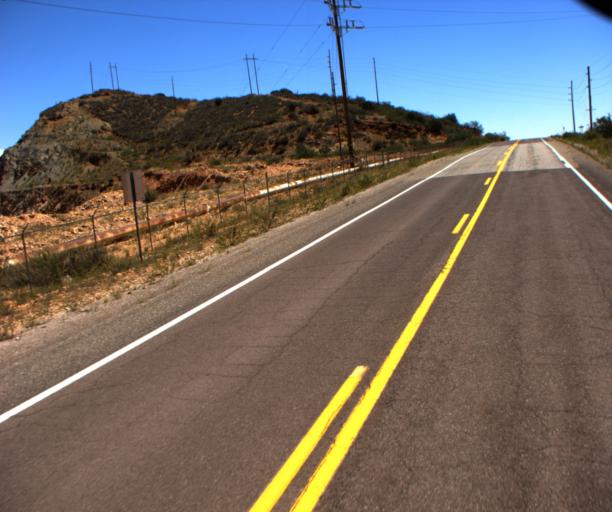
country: US
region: Arizona
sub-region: Greenlee County
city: Morenci
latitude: 33.0730
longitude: -109.3780
